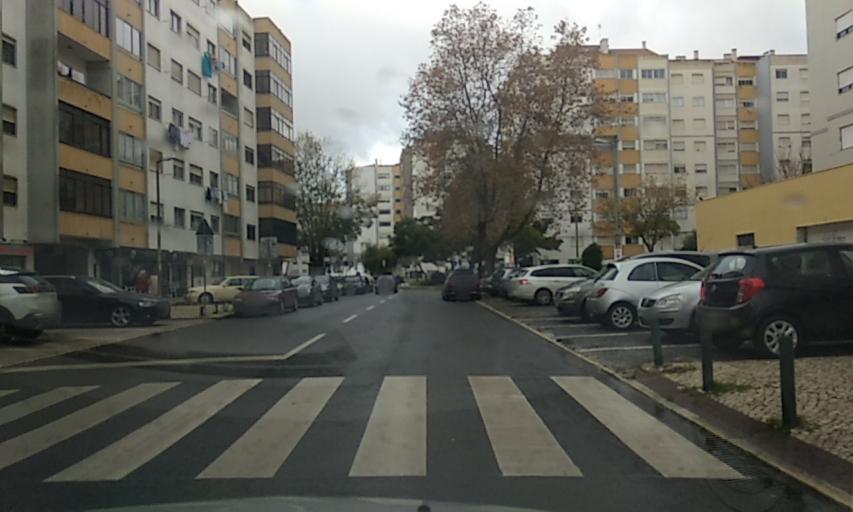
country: PT
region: Lisbon
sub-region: Sintra
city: Cacem
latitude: 38.7546
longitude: -9.2852
